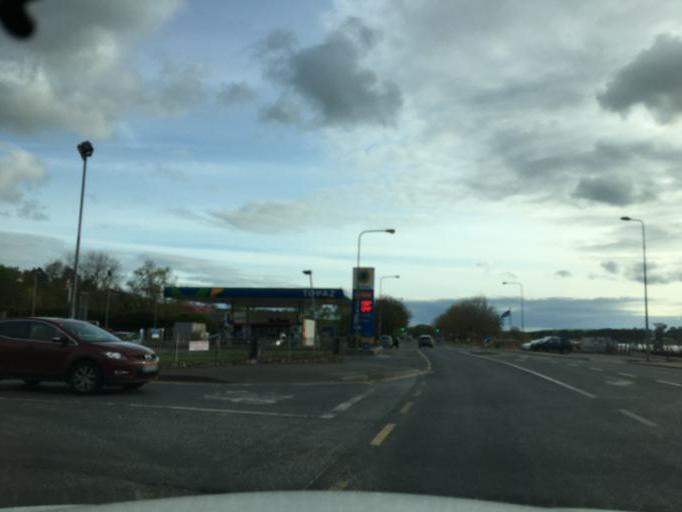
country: IE
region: Leinster
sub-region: Loch Garman
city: New Ross
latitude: 52.3921
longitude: -6.9493
